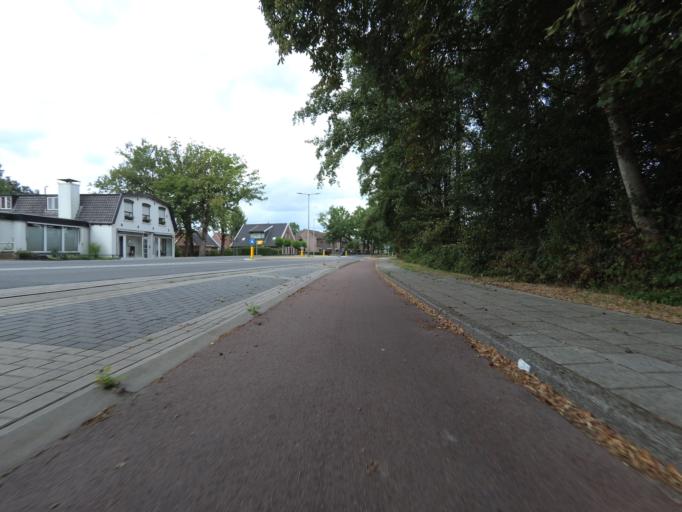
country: NL
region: Overijssel
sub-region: Gemeente Enschede
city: Enschede
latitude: 52.2513
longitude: 6.9152
